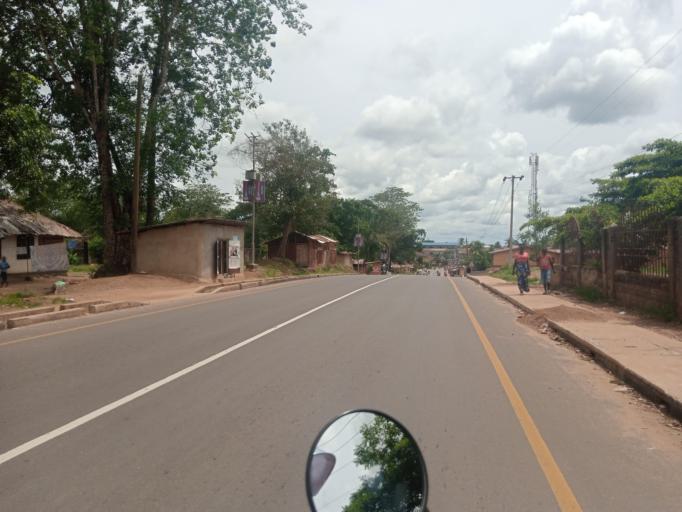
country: SL
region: Southern Province
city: Bo
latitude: 7.9570
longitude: -11.7281
